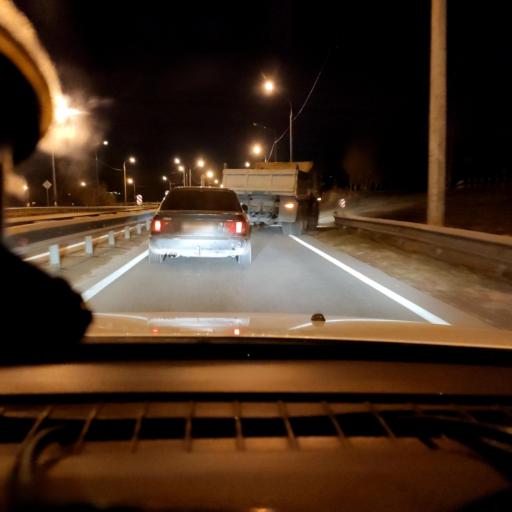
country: RU
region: Samara
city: Volzhskiy
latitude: 53.4340
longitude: 50.1202
